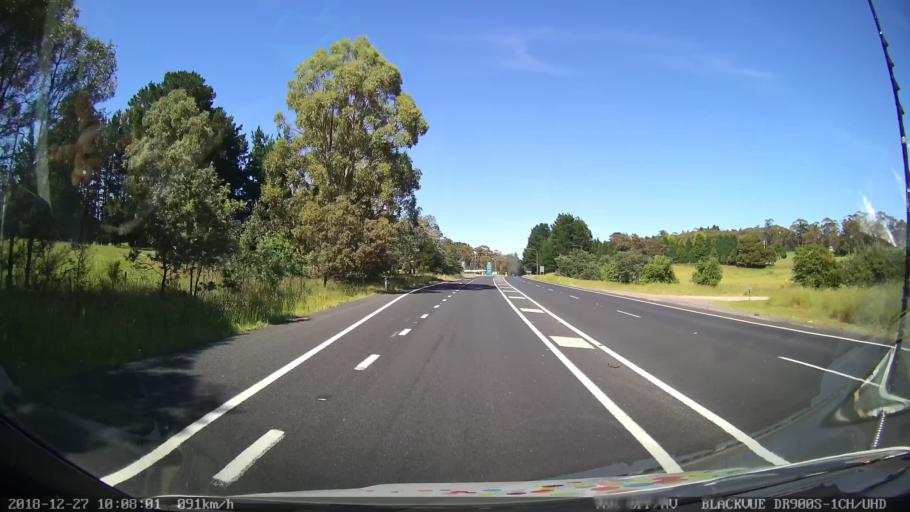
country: AU
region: New South Wales
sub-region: Lithgow
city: Portland
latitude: -33.4448
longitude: 149.8319
